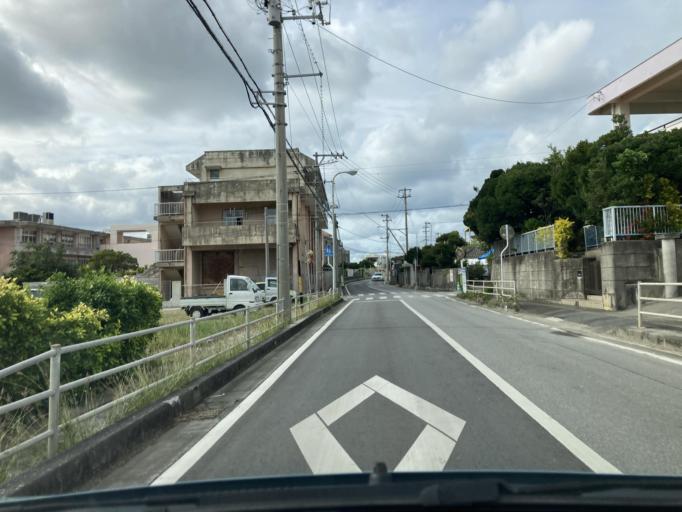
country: JP
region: Okinawa
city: Itoman
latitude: 26.1036
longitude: 127.6912
